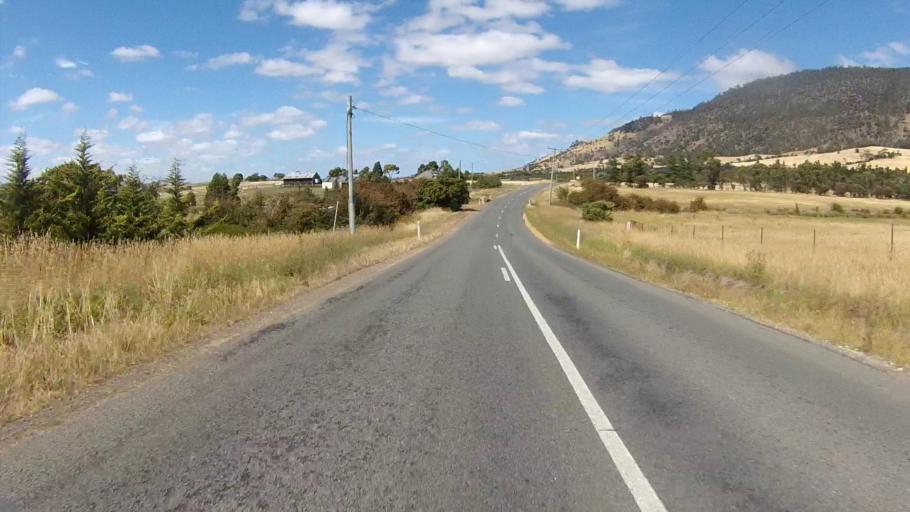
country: AU
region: Tasmania
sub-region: Sorell
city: Sorell
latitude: -42.6210
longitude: 147.4297
